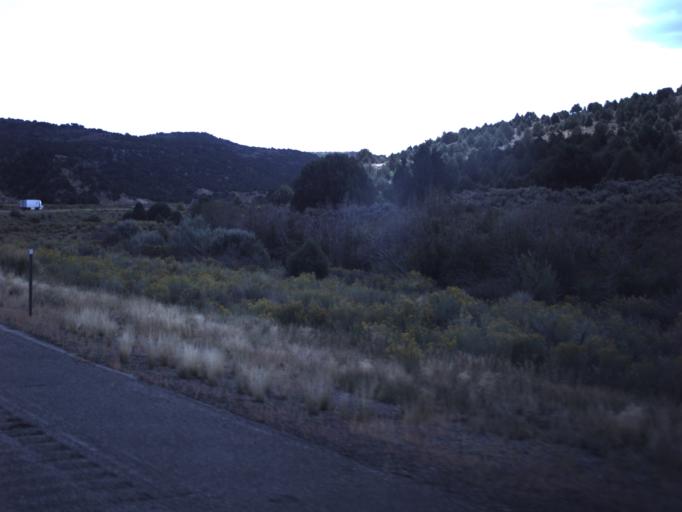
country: US
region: Utah
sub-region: Sevier County
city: Salina
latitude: 38.8503
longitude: -111.5428
